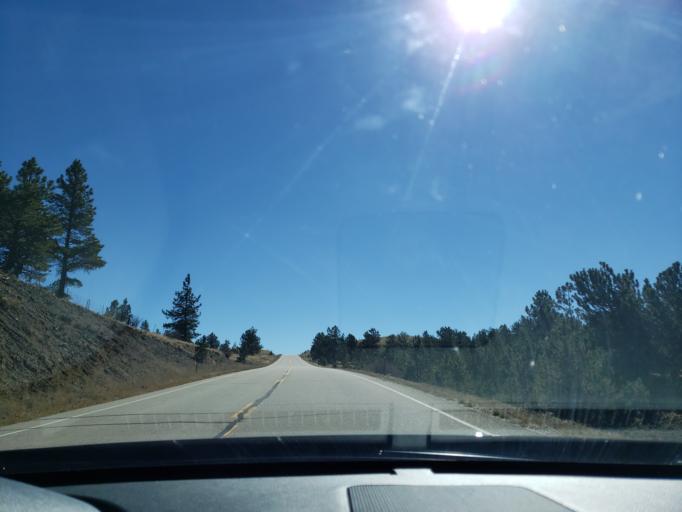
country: US
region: Colorado
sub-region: Chaffee County
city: Buena Vista
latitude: 38.8944
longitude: -105.6900
